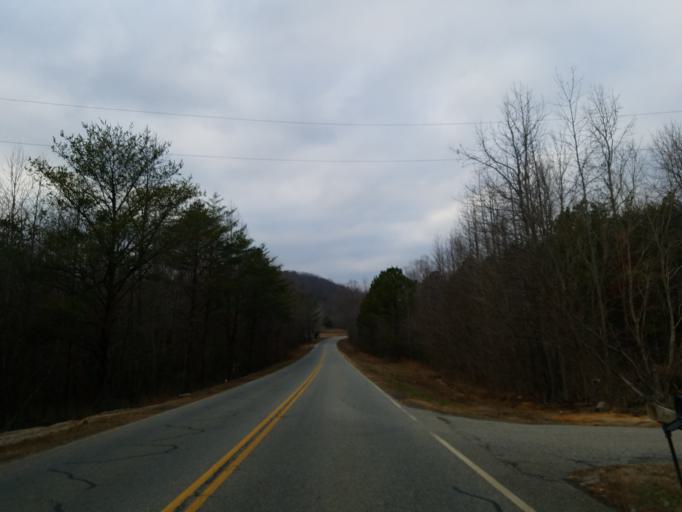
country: US
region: Georgia
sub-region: Bartow County
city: Rydal
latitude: 34.3465
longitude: -84.6600
